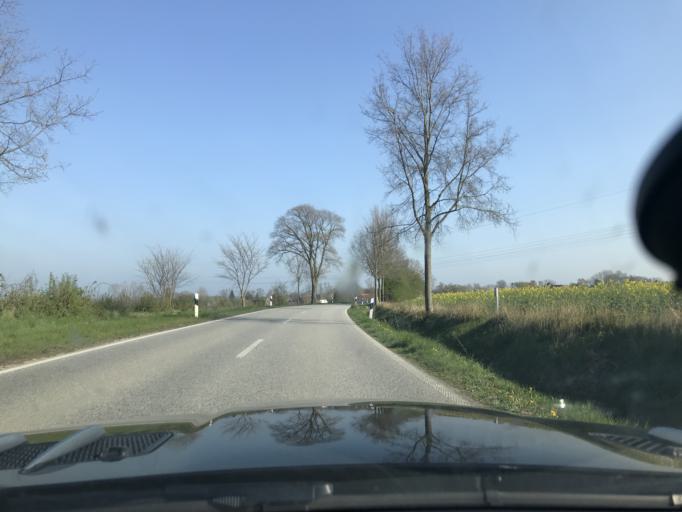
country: DE
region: Schleswig-Holstein
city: Neukirchen
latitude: 54.3640
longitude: 11.0314
